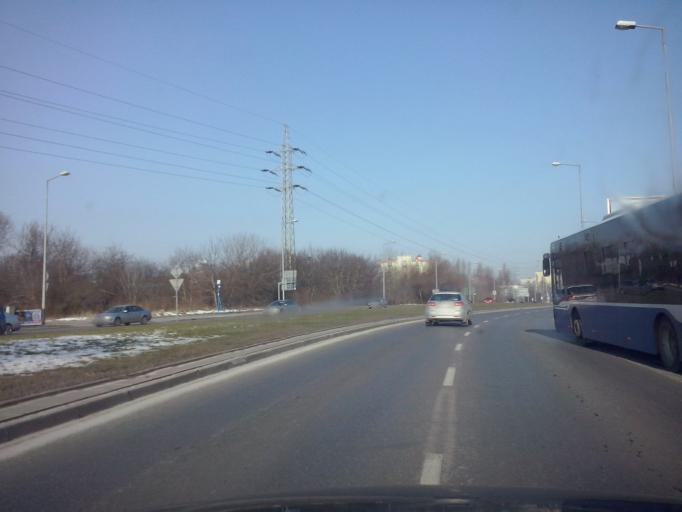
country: PL
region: Lesser Poland Voivodeship
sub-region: Krakow
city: Krakow
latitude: 50.0676
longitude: 20.0047
